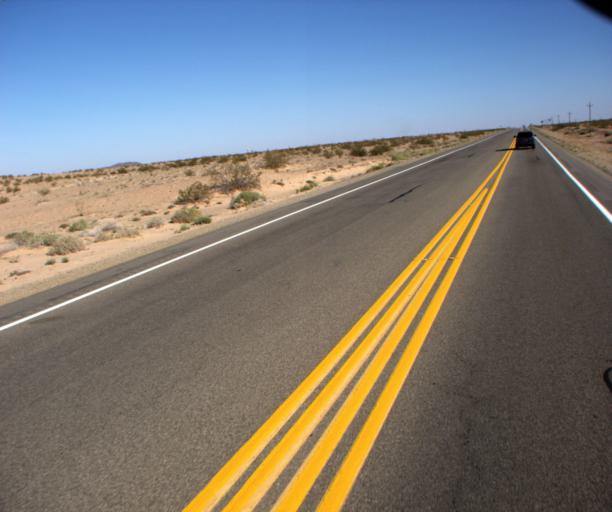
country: US
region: Arizona
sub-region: Yuma County
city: Fortuna Foothills
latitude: 32.8101
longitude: -114.3797
